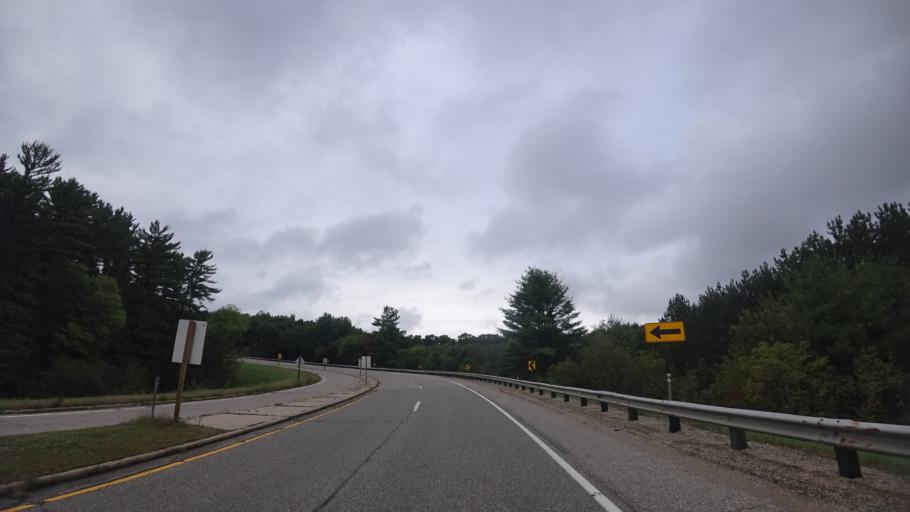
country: US
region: Wisconsin
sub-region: Sauk County
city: Lake Delton
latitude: 43.6242
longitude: -89.8062
